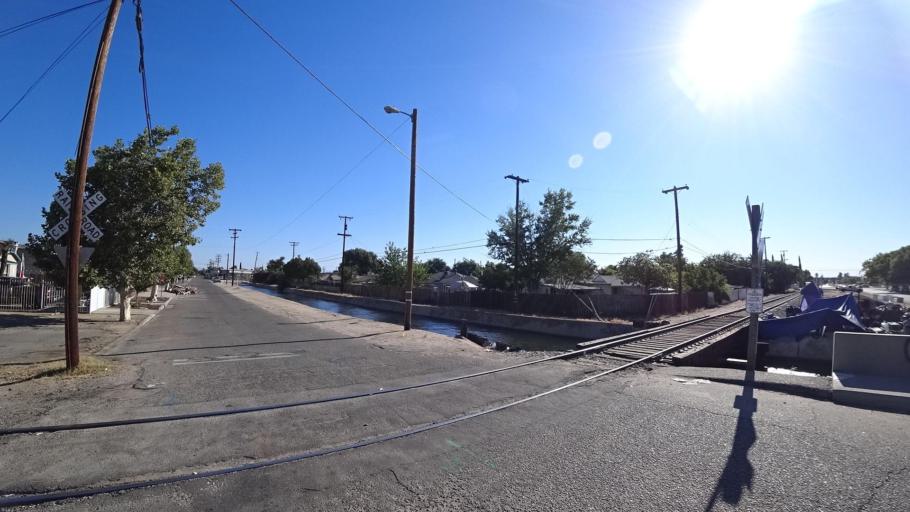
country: US
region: California
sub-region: Fresno County
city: Fresno
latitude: 36.7615
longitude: -119.7838
